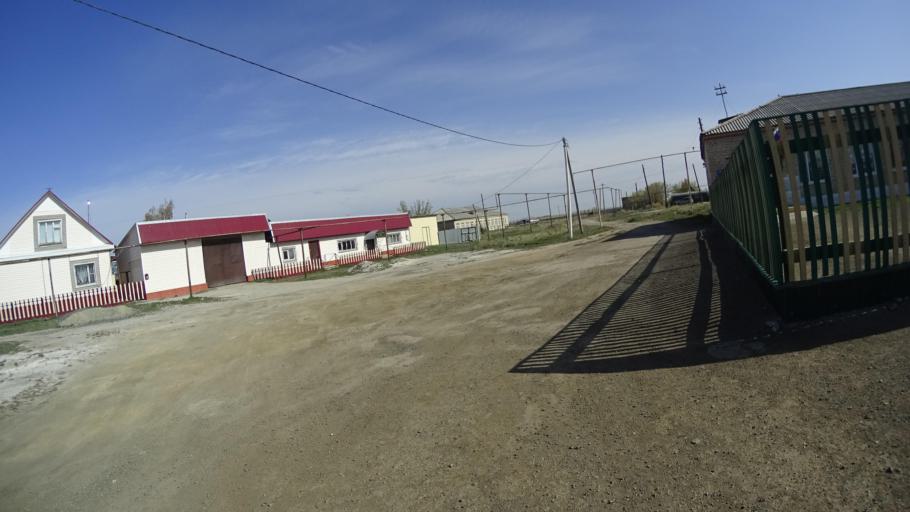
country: RU
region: Chelyabinsk
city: Chesma
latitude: 53.7957
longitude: 61.0334
